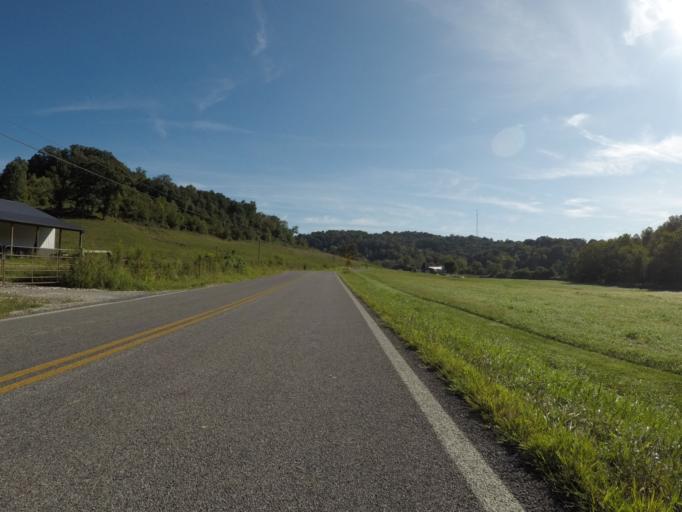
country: US
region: West Virginia
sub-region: Cabell County
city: Huntington
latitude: 38.4944
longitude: -82.4926
